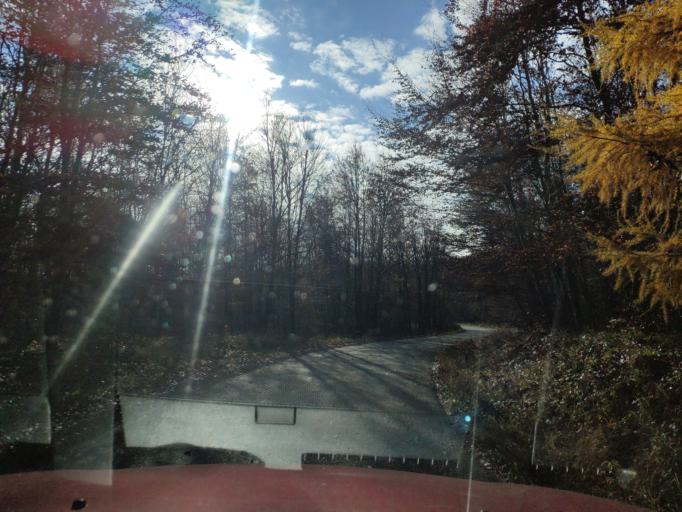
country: SK
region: Kosicky
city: Secovce
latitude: 48.6231
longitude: 21.4618
